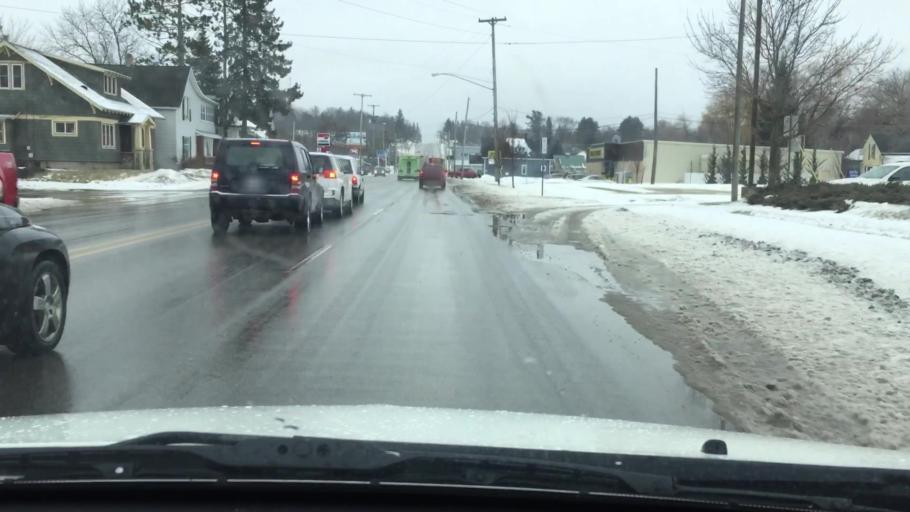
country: US
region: Michigan
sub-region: Wexford County
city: Cadillac
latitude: 44.2448
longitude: -85.3965
